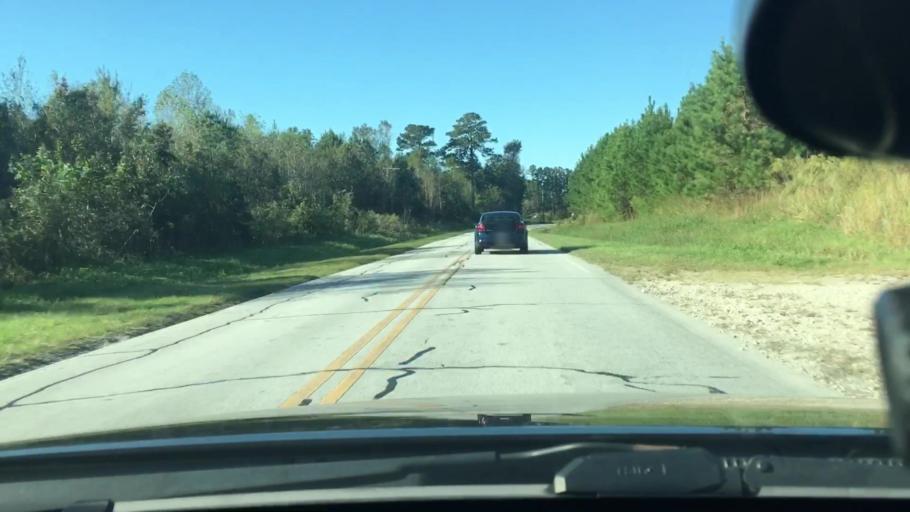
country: US
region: North Carolina
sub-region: Craven County
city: Vanceboro
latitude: 35.2827
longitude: -77.1538
